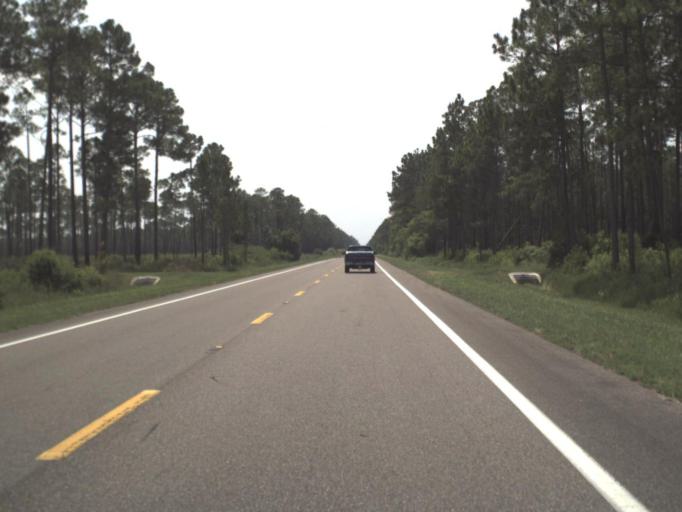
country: US
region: Florida
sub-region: Putnam County
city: Palatka
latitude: 29.4570
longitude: -81.7382
